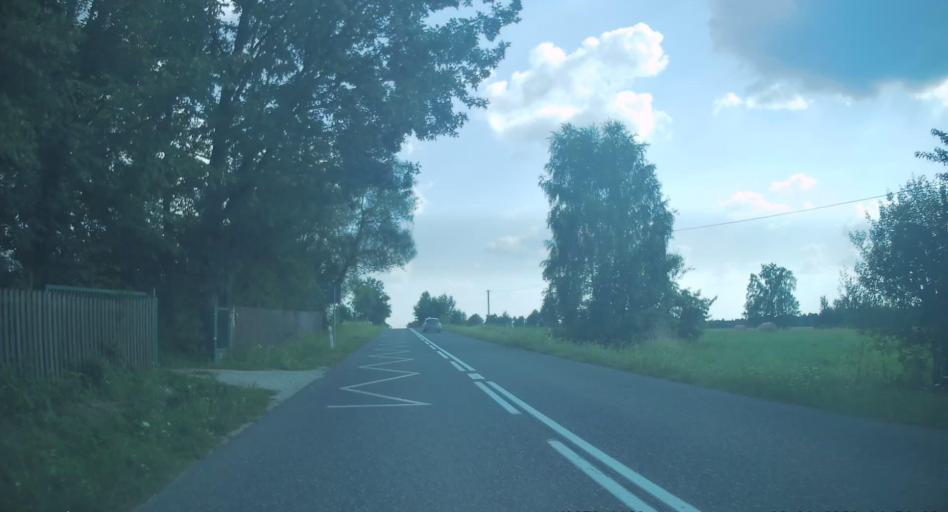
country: PL
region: Swietokrzyskie
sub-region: Powiat kielecki
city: Lopuszno
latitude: 50.9190
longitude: 20.2421
